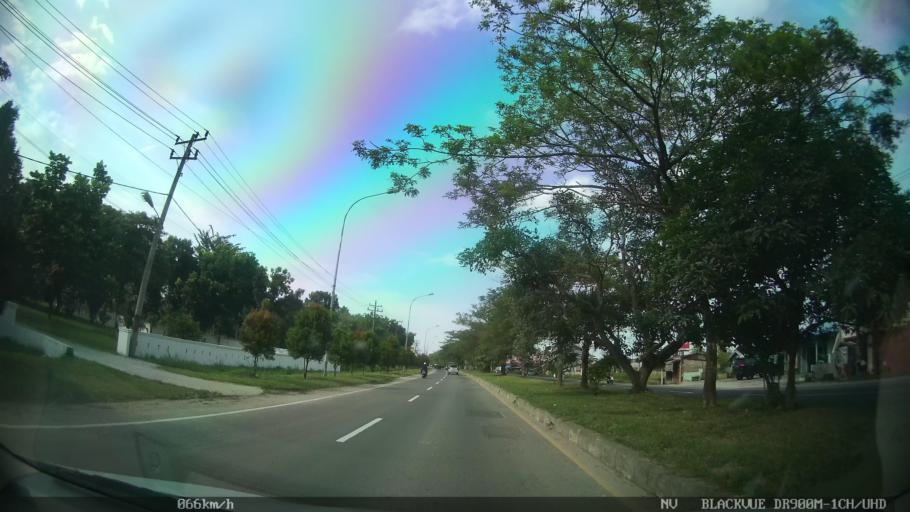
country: ID
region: North Sumatra
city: Percut
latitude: 3.5750
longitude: 98.8000
